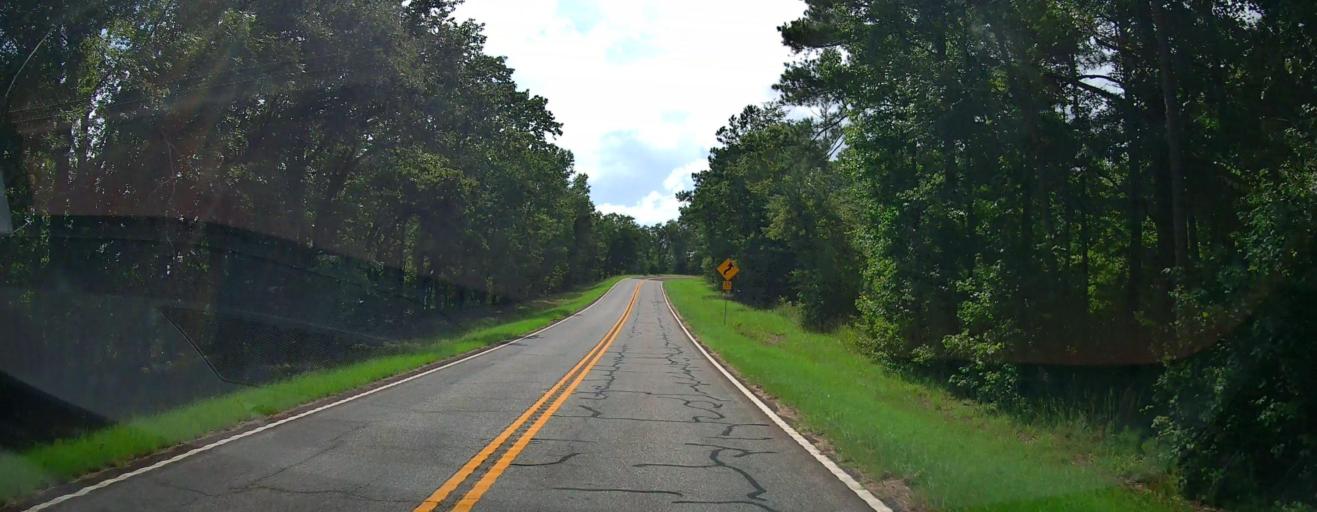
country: US
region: Georgia
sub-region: Talbot County
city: Sardis
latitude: 32.8487
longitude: -84.7035
